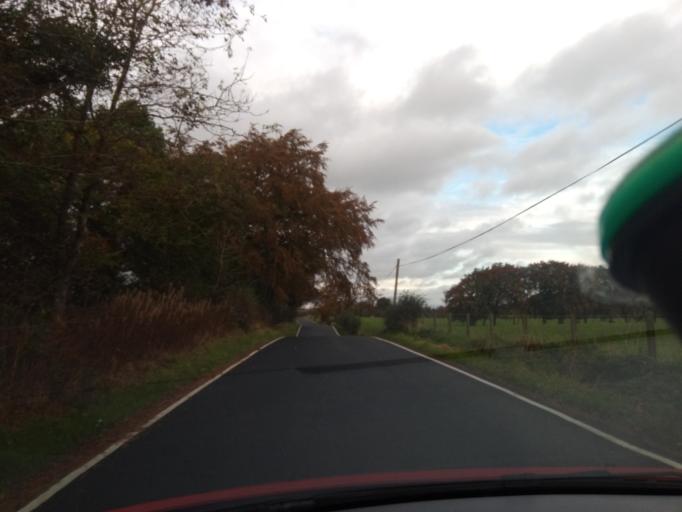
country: GB
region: Scotland
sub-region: West Lothian
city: Blackburn
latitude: 55.8337
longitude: -3.6121
